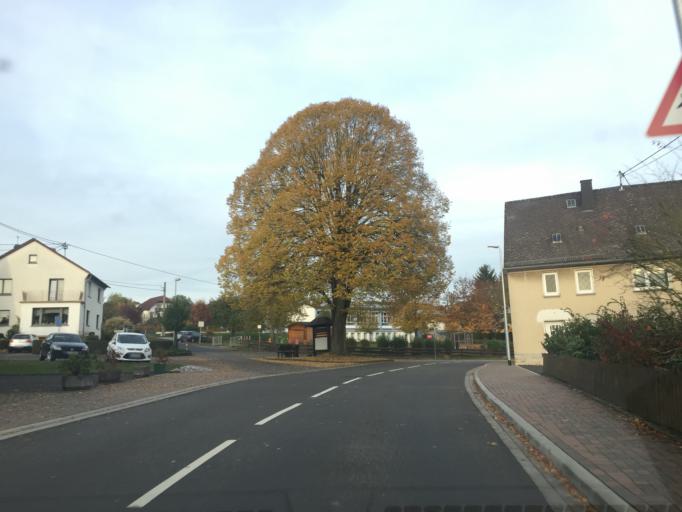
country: DE
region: Rheinland-Pfalz
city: Weroth
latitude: 50.4597
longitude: 7.9494
